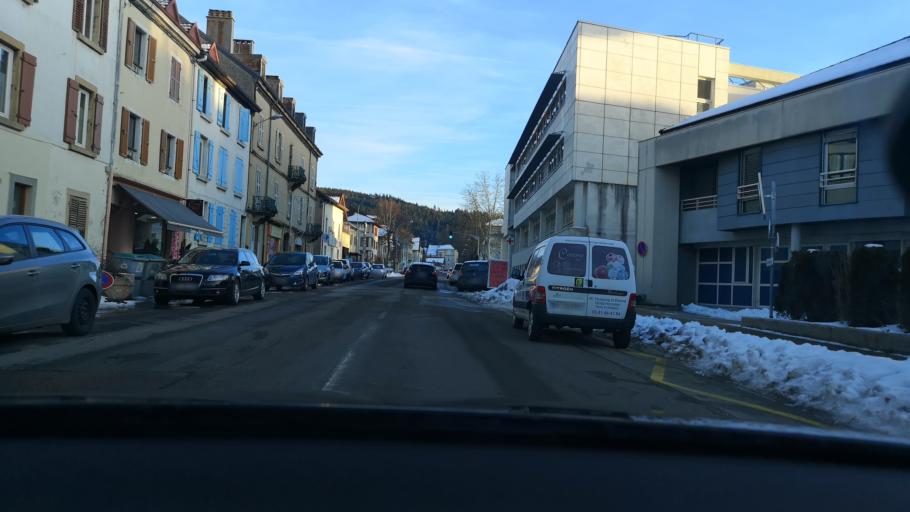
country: FR
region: Franche-Comte
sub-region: Departement du Doubs
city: Pontarlier
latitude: 46.9012
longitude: 6.3603
